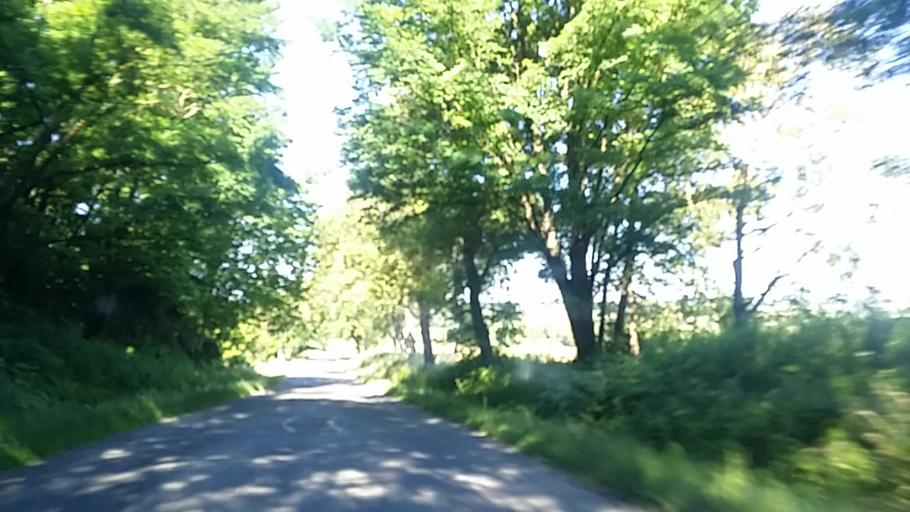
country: HU
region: Zala
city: Zalaegerszeg
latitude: 46.8692
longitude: 16.7272
